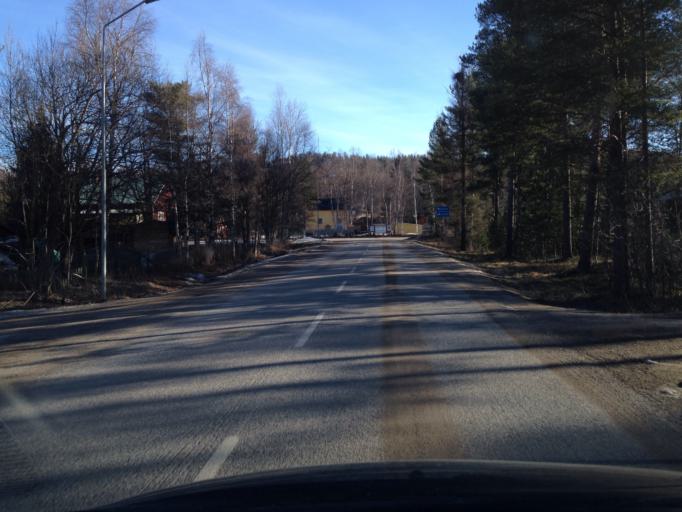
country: SE
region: Jaemtland
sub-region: Harjedalens Kommun
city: Sveg
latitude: 62.1559
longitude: 13.8895
